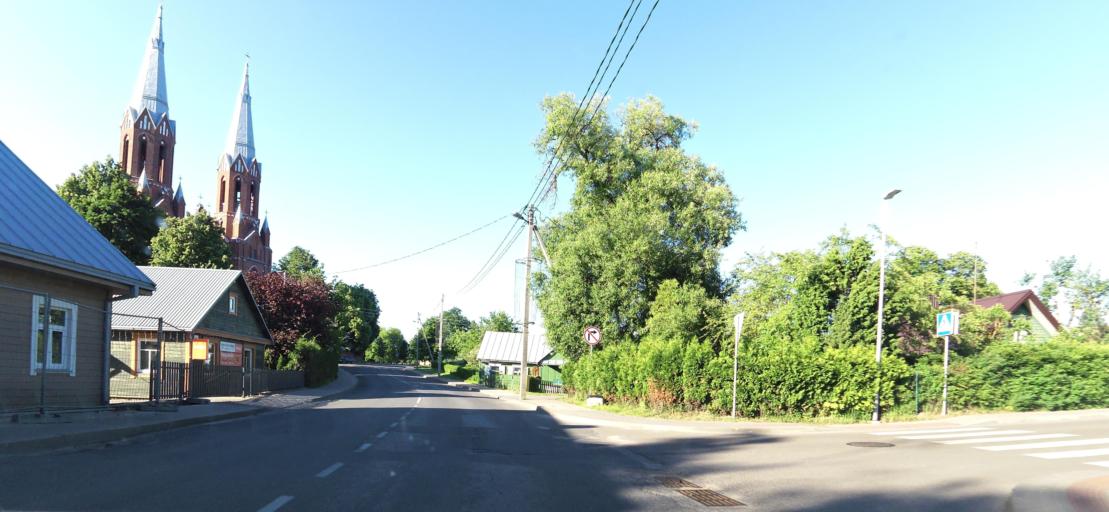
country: LT
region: Utenos apskritis
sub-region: Anyksciai
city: Anyksciai
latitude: 55.5230
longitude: 25.1003
